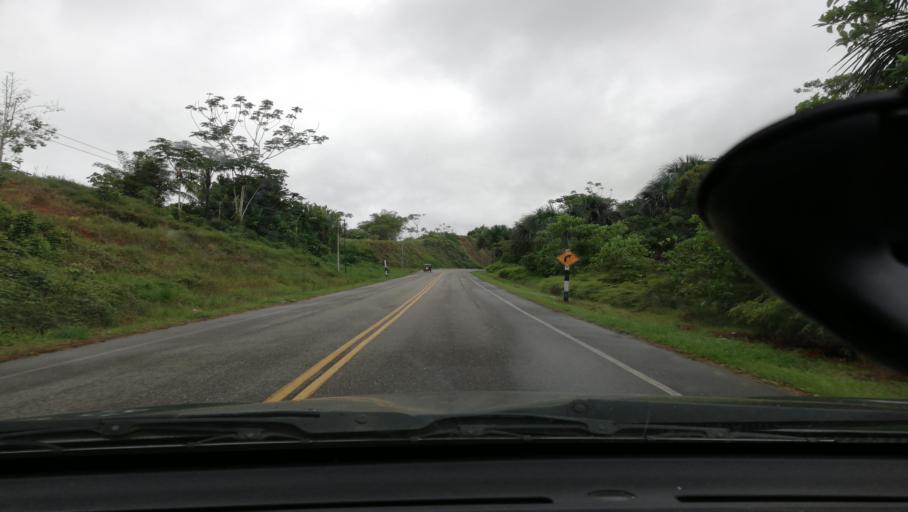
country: PE
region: Loreto
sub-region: Provincia de Loreto
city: Nauta
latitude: -4.4806
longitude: -73.5952
